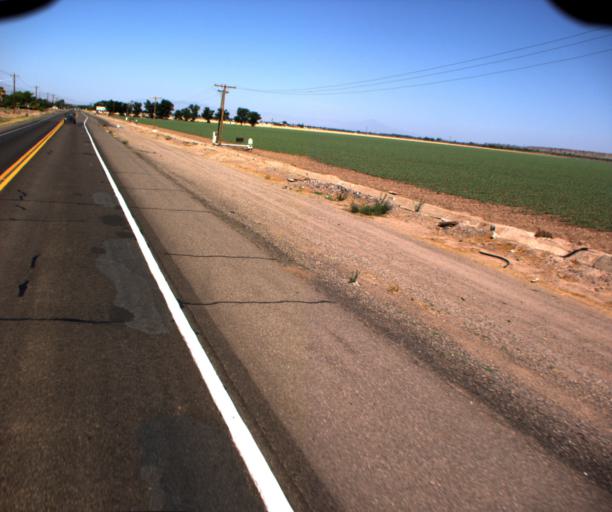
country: US
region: Arizona
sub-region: Graham County
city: Safford
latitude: 32.8166
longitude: -109.6499
